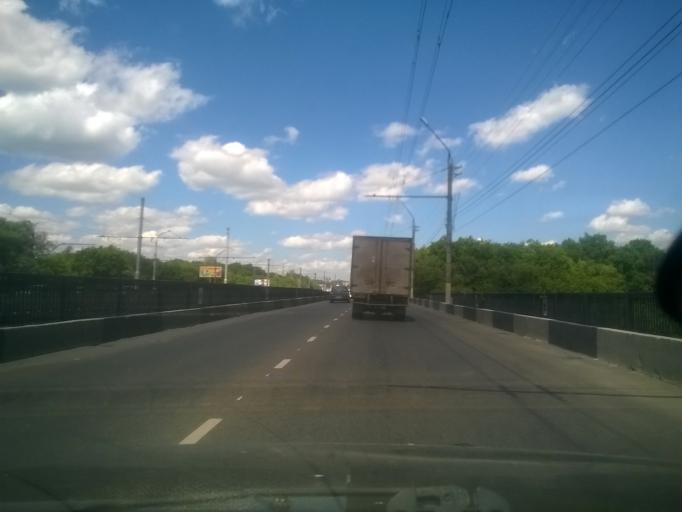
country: RU
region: Kursk
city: Kursk
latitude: 51.6802
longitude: 36.1486
